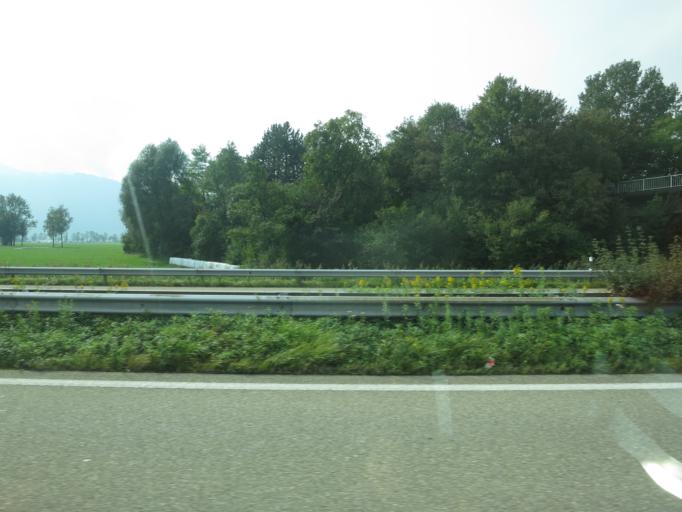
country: CH
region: Schwyz
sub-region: Bezirk March
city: Tuggen
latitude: 47.2015
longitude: 8.9677
